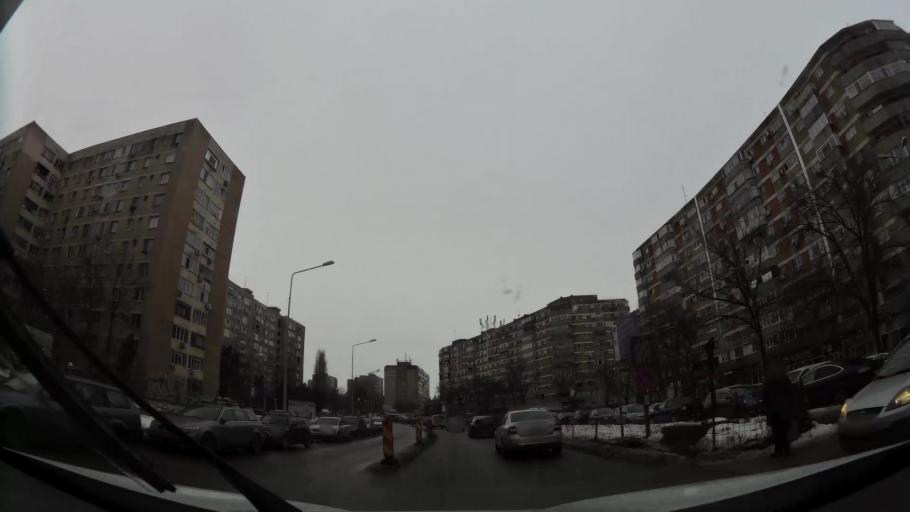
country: RO
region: Ilfov
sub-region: Comuna Chiajna
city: Rosu
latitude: 44.4190
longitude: 26.0202
